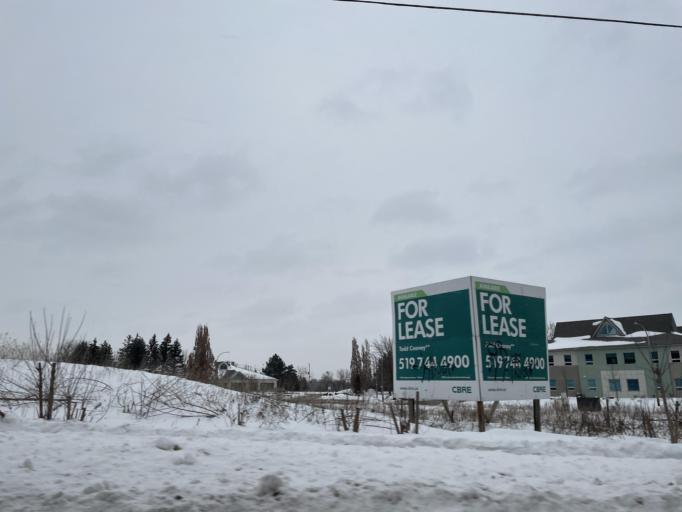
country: CA
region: Ontario
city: Waterloo
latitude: 43.4768
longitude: -80.4825
